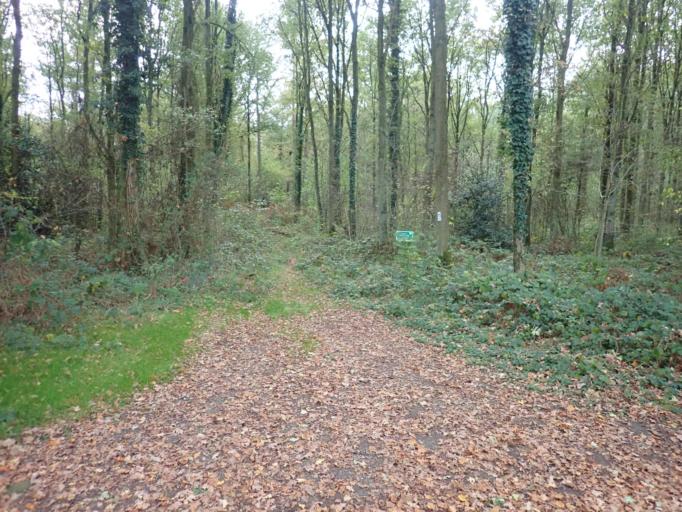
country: BE
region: Flanders
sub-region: Provincie Antwerpen
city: Sint-Katelijne-Waver
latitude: 51.0817
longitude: 4.5826
